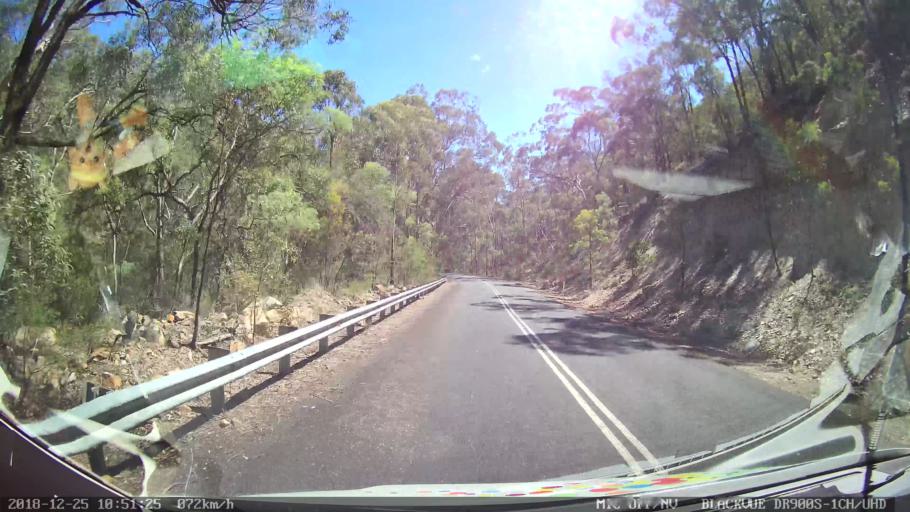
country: AU
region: New South Wales
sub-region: Upper Hunter Shire
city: Merriwa
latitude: -32.4371
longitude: 150.2693
